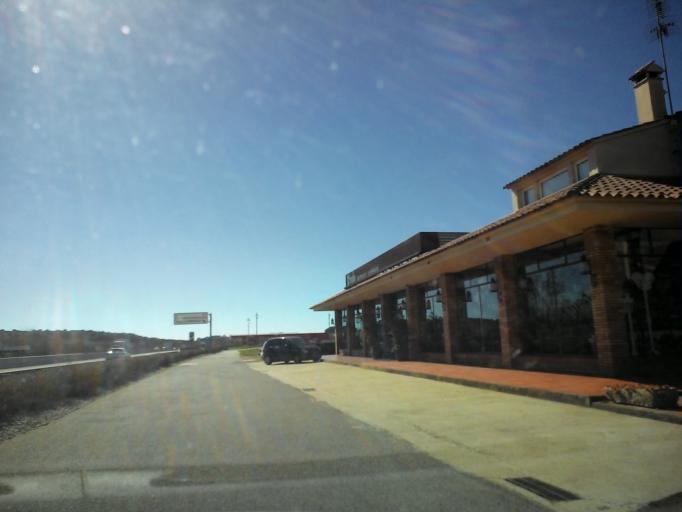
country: ES
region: Catalonia
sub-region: Provincia de Girona
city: Palamos
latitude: 41.8742
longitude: 3.1388
